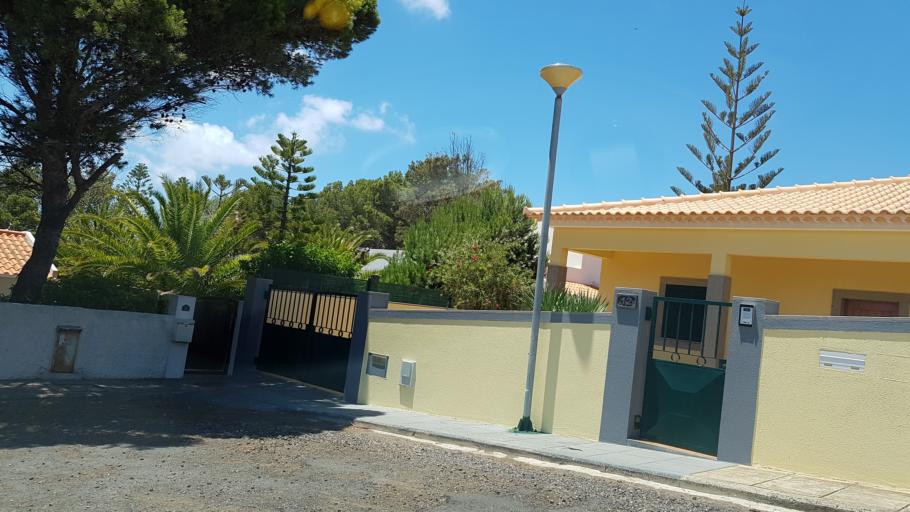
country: PT
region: Madeira
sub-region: Porto Santo
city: Vila de Porto Santo
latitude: 33.0606
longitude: -16.3527
